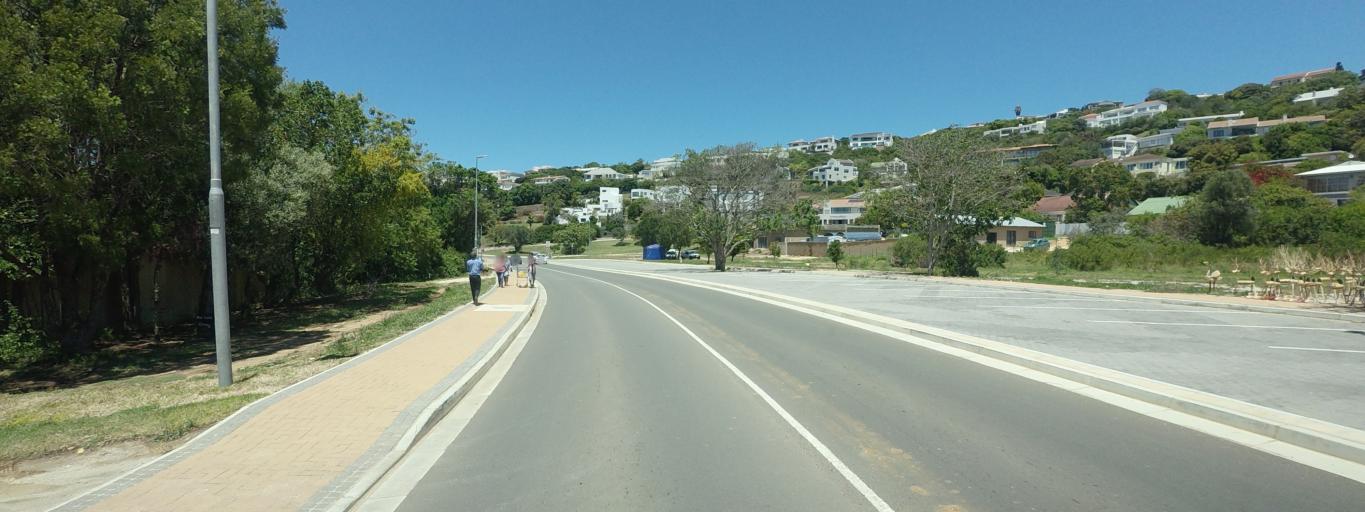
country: ZA
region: Western Cape
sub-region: Eden District Municipality
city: Plettenberg Bay
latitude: -34.0461
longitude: 23.3688
